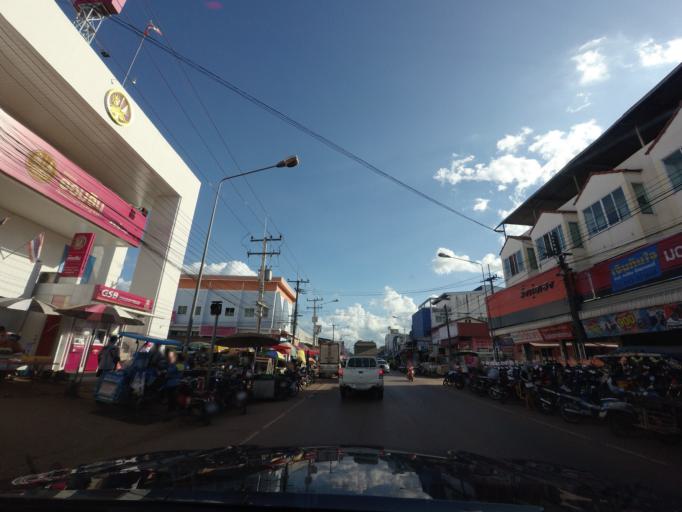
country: TH
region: Changwat Udon Thani
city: Ban Dung
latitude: 17.6975
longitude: 103.2591
